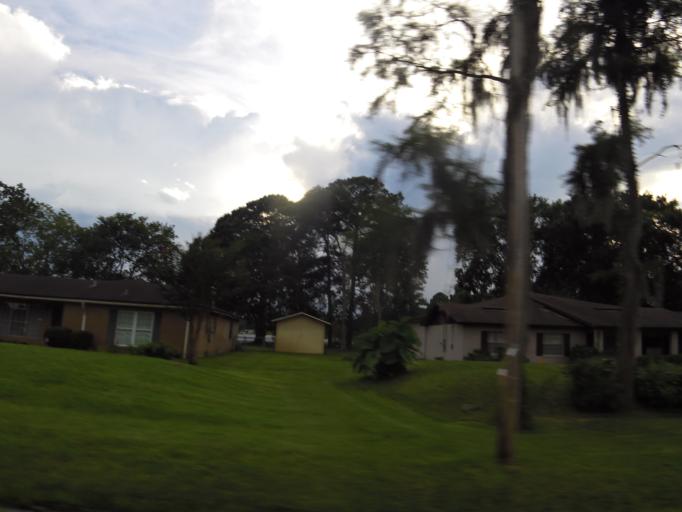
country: US
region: Florida
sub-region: Duval County
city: Jacksonville
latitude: 30.3286
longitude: -81.7899
